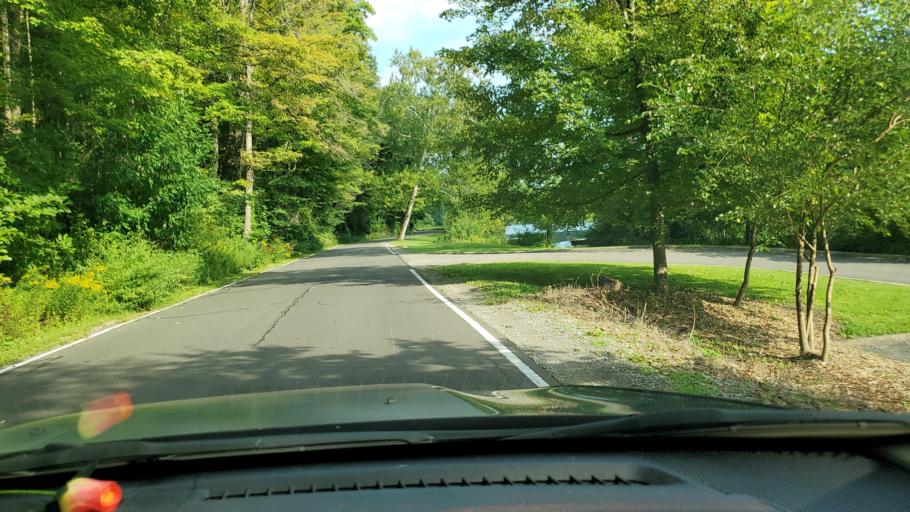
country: US
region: Ohio
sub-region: Mahoning County
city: Youngstown
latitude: 41.0901
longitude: -80.6764
